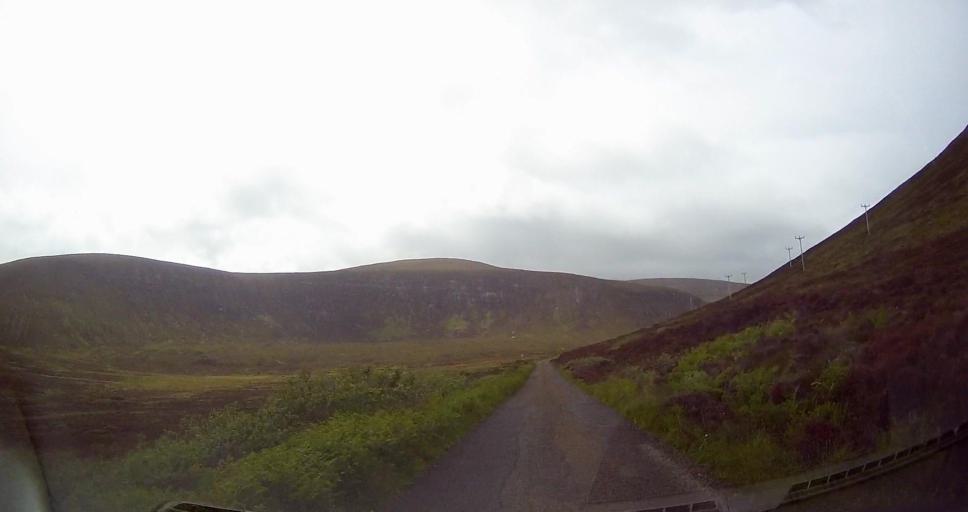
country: GB
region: Scotland
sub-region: Orkney Islands
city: Stromness
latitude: 58.8941
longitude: -3.3144
